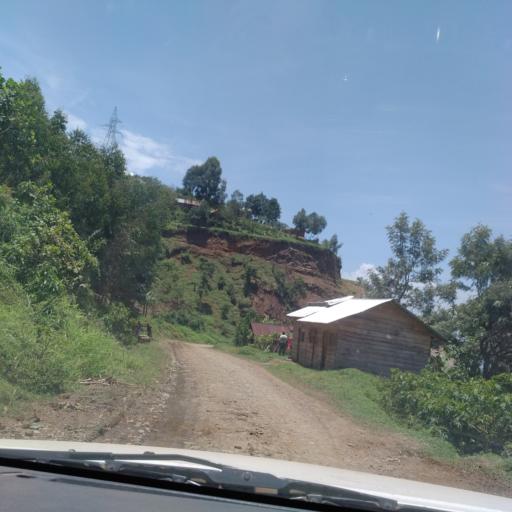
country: CD
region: Nord Kivu
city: Sake
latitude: -1.9126
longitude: 28.9595
